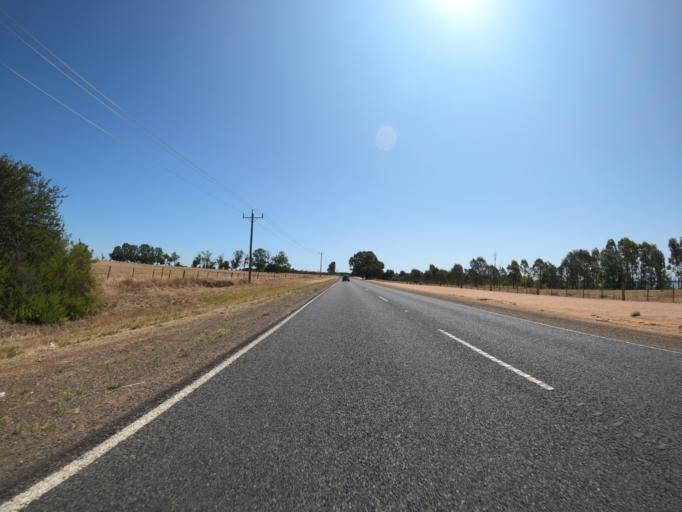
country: AU
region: Victoria
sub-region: Moira
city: Yarrawonga
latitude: -36.0271
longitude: 146.0814
